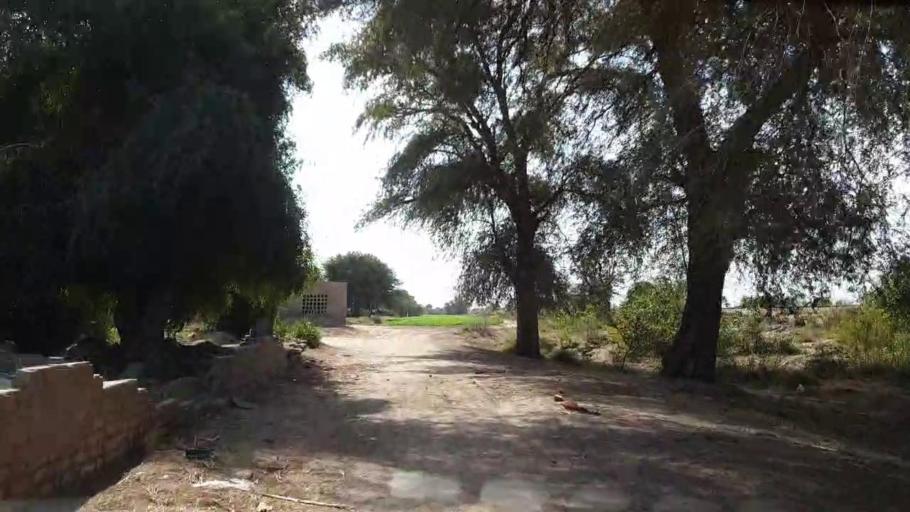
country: PK
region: Sindh
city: Matiari
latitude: 25.5431
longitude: 68.5449
